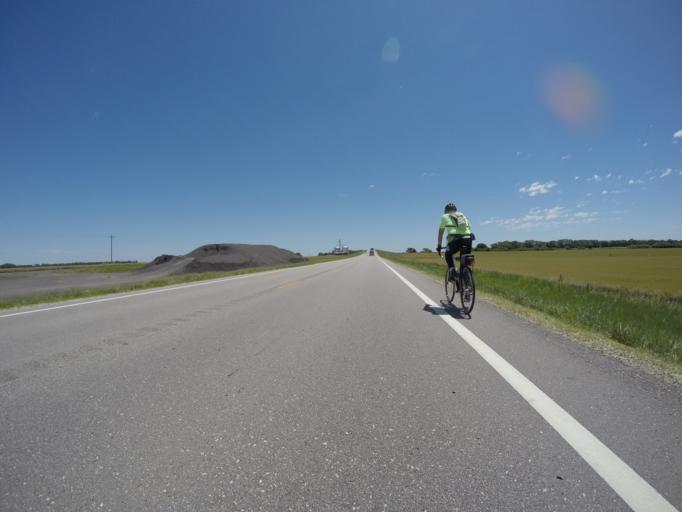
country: US
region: Kansas
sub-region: Republic County
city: Belleville
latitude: 39.8127
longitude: -97.7208
